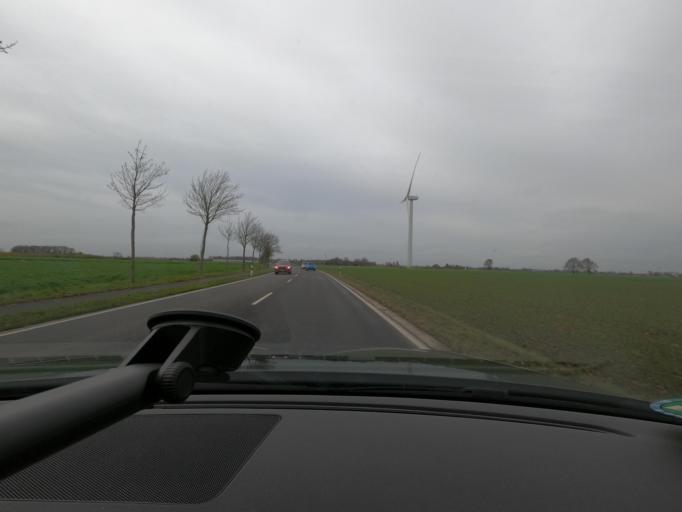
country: DE
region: North Rhine-Westphalia
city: Tonisvorst
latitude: 51.3450
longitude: 6.4821
